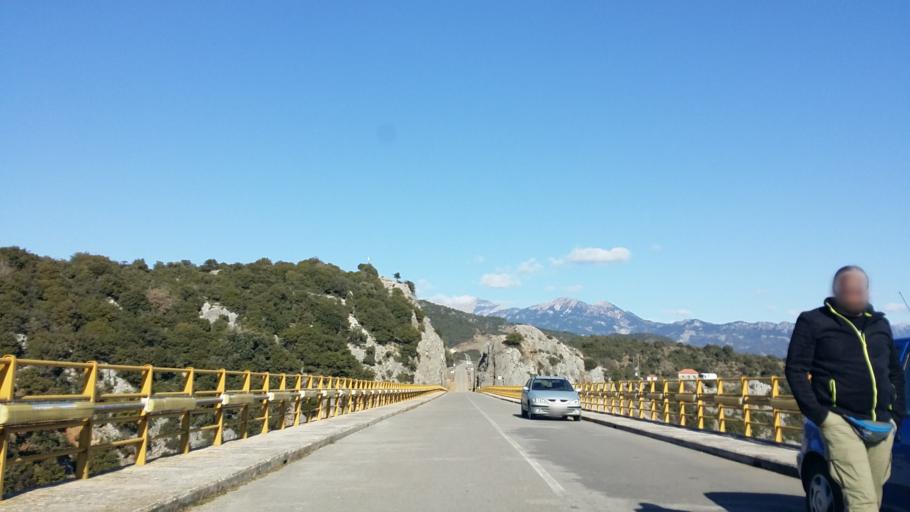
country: GR
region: Central Greece
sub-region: Nomos Evrytanias
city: Kerasochori
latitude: 38.9706
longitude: 21.4913
